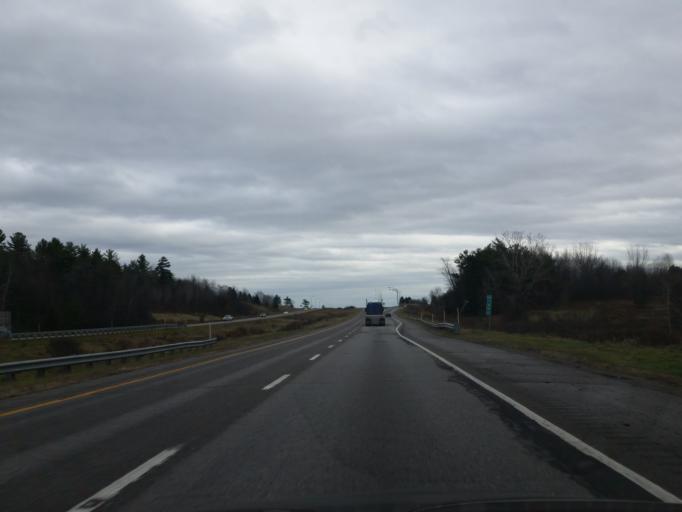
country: CA
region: Quebec
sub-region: Outaouais
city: Gatineau
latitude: 45.5110
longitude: -75.6230
